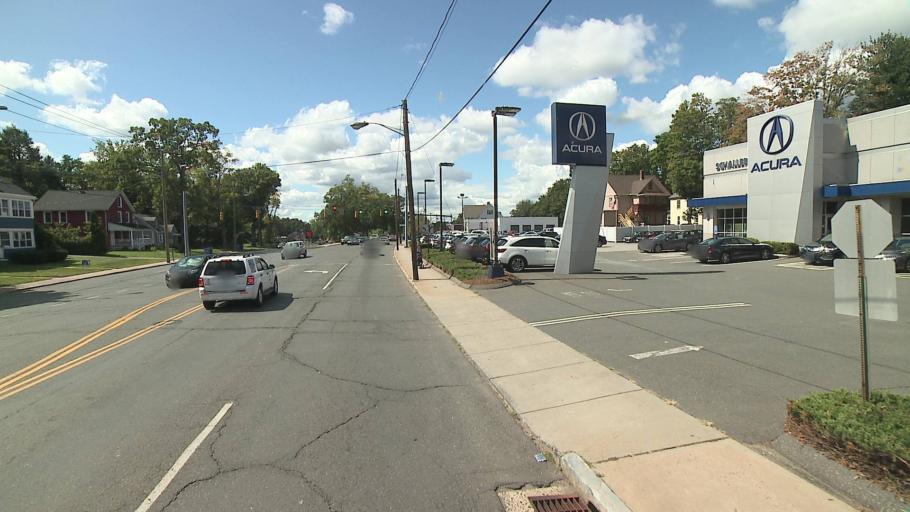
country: US
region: Connecticut
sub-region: Hartford County
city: Manchester
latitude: 41.7725
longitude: -72.5343
